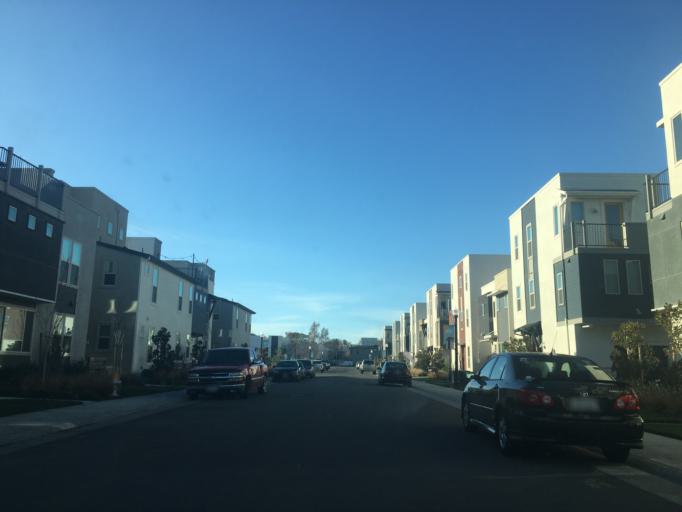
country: US
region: California
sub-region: Sacramento County
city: Sacramento
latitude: 38.5638
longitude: -121.5088
